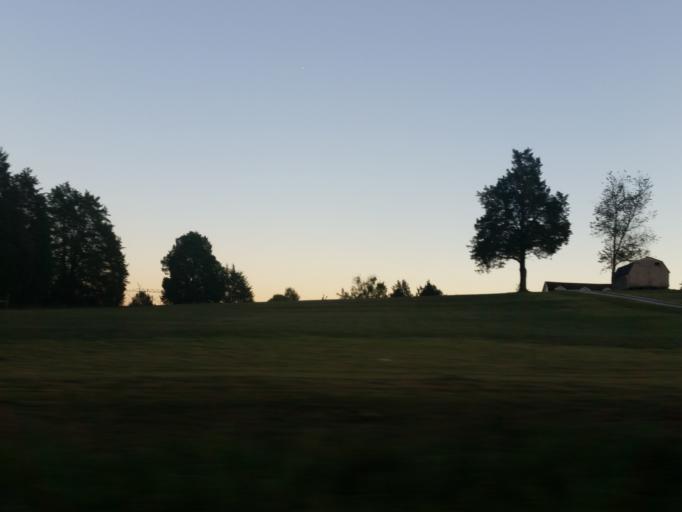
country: US
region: Tennessee
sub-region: Union County
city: Condon
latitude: 36.1305
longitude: -83.8274
